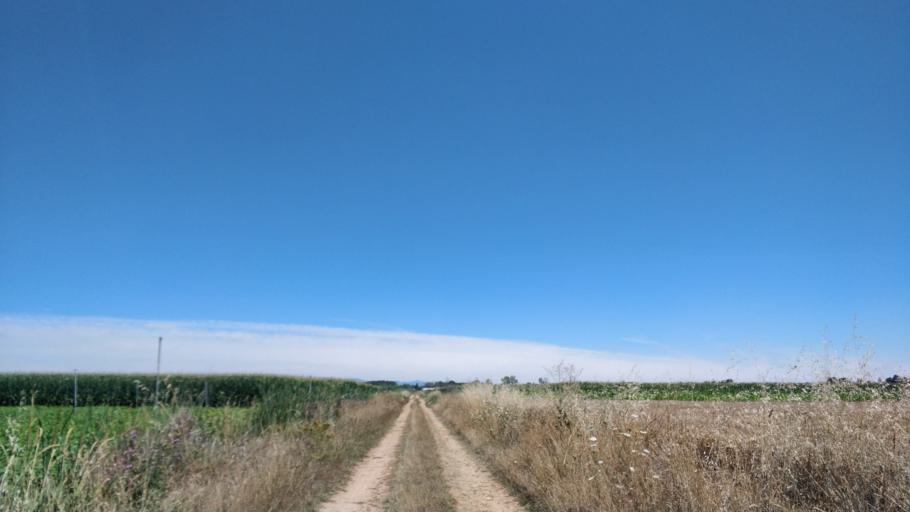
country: ES
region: Castille and Leon
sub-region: Provincia de Leon
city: Bustillo del Paramo
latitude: 42.4658
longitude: -5.8147
